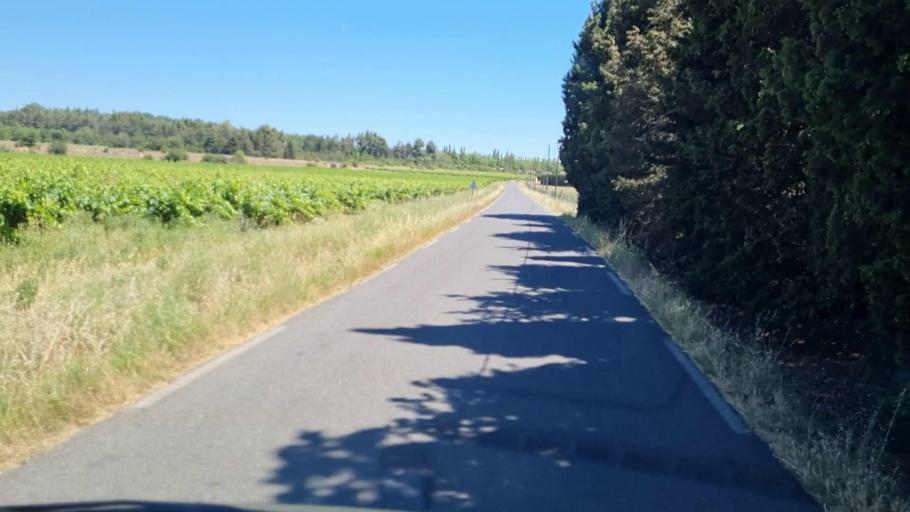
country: FR
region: Languedoc-Roussillon
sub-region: Departement du Gard
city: Le Cailar
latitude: 43.6705
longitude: 4.2576
